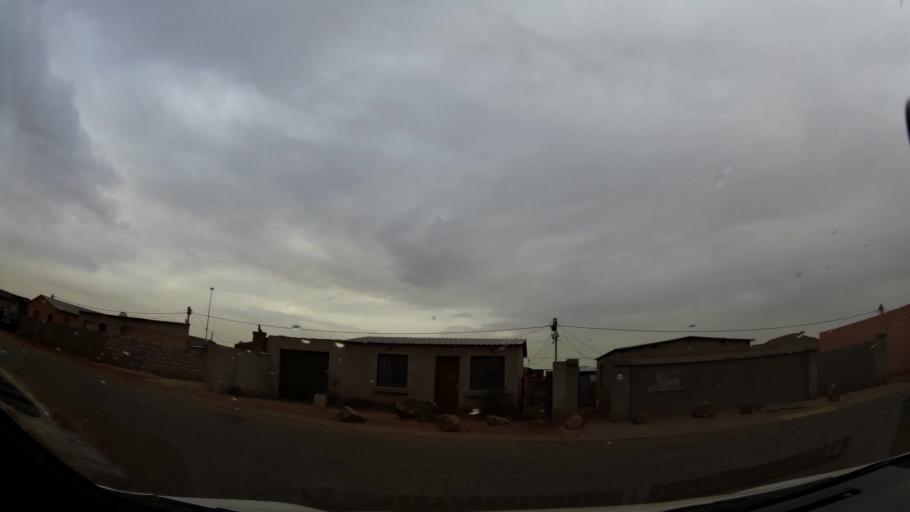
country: ZA
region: Gauteng
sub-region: Ekurhuleni Metropolitan Municipality
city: Germiston
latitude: -26.3865
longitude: 28.1747
